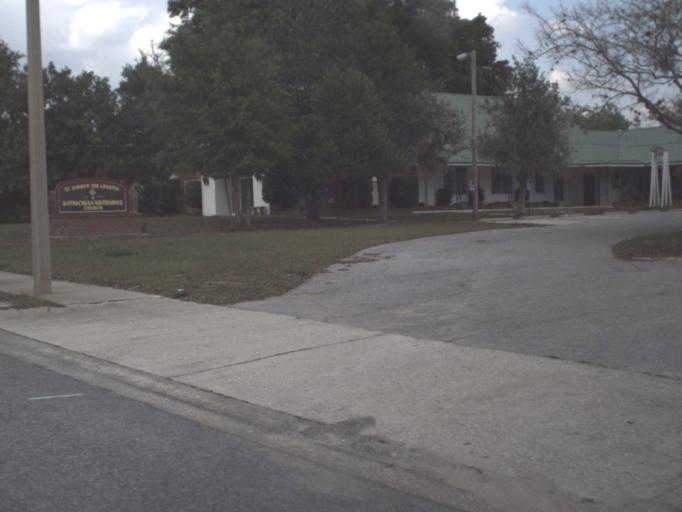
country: US
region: Florida
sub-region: Lake County
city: Eustis
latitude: 28.8261
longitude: -81.6854
